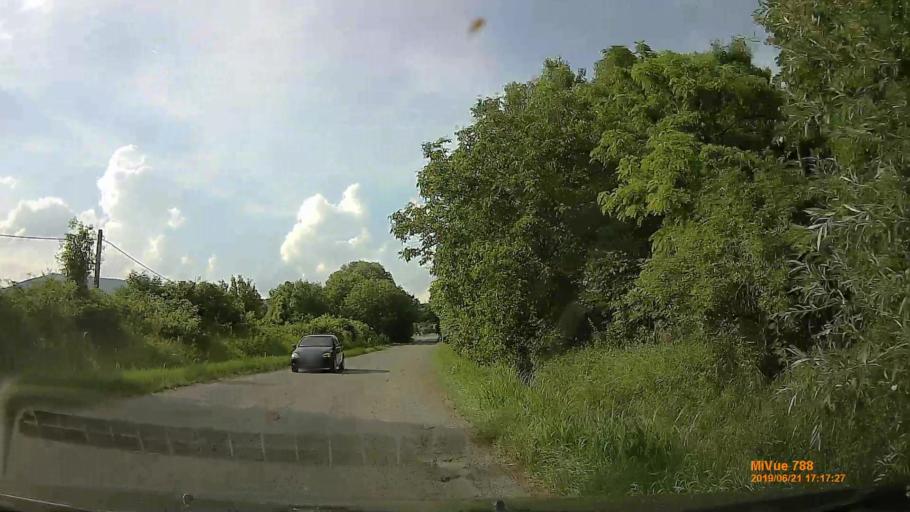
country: HU
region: Baranya
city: Pecsvarad
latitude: 46.1506
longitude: 18.4239
